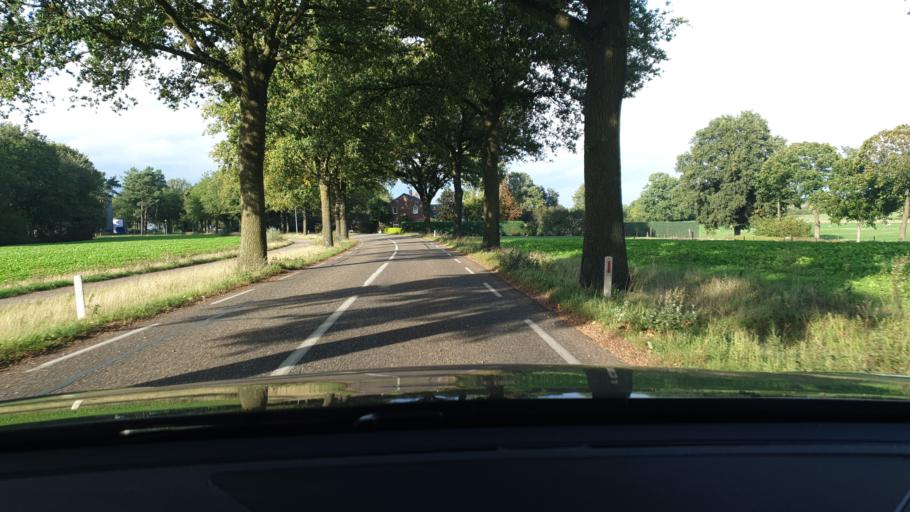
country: NL
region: Limburg
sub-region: Gemeente Venlo
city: Arcen
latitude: 51.4710
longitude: 6.1666
